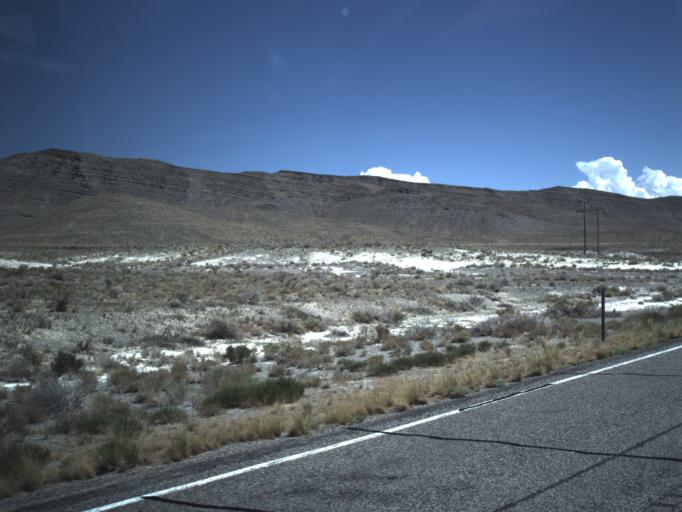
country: US
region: Utah
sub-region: Beaver County
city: Milford
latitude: 39.0370
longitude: -113.3941
